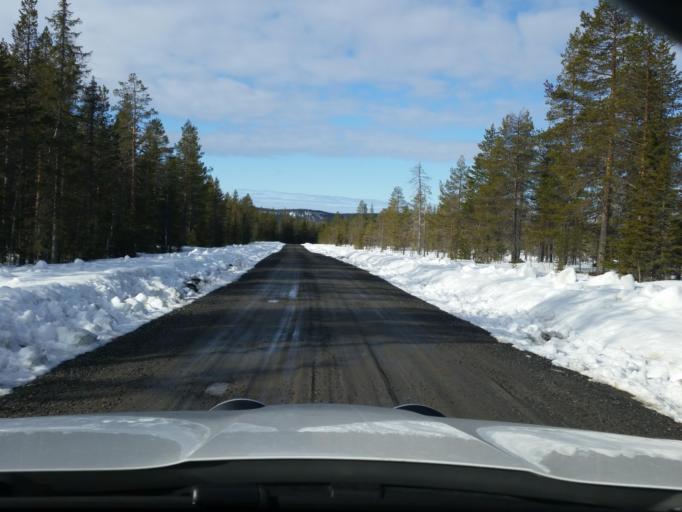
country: SE
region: Vaesterbotten
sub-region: Skelleftea Kommun
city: Storvik
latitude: 65.5059
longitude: 20.3692
